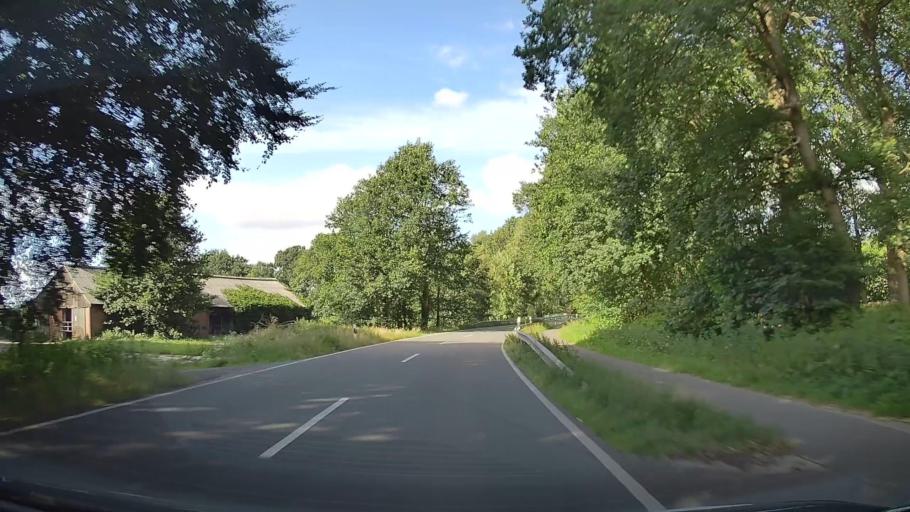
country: DE
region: Lower Saxony
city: Bosel
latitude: 52.9602
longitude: 7.9077
